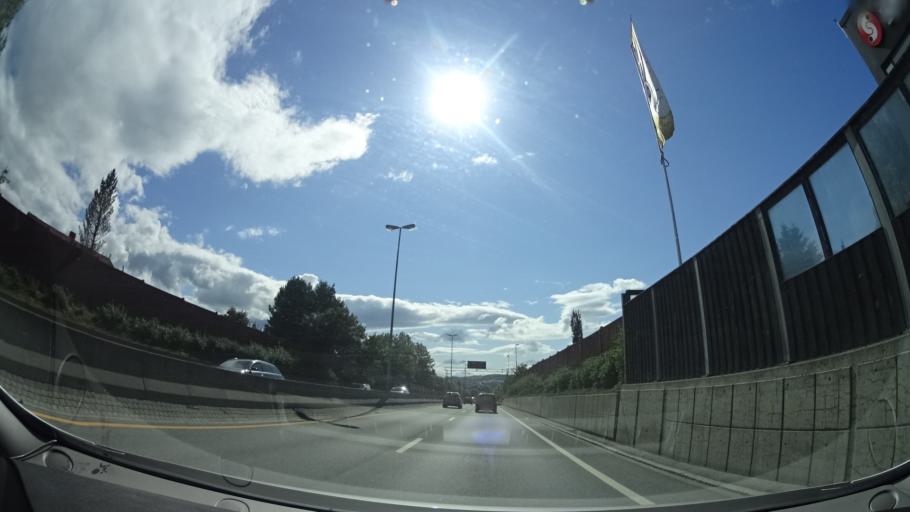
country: NO
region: Sor-Trondelag
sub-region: Trondheim
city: Trondheim
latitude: 63.4059
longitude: 10.4168
